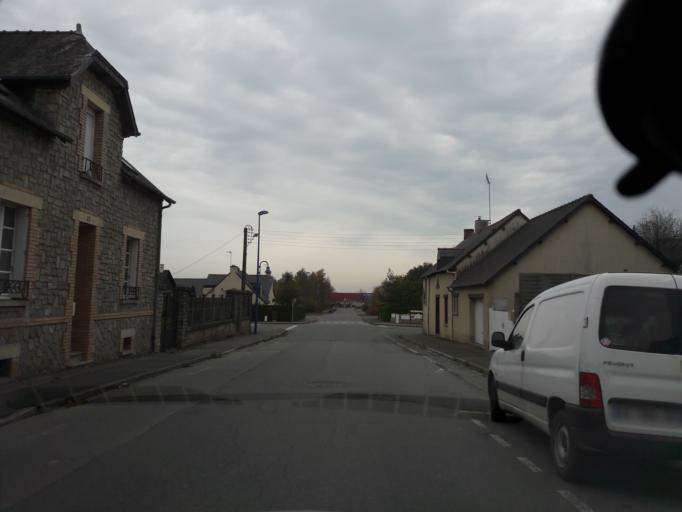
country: FR
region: Brittany
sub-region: Departement d'Ille-et-Vilaine
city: Janze
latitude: 47.9593
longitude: -1.4923
